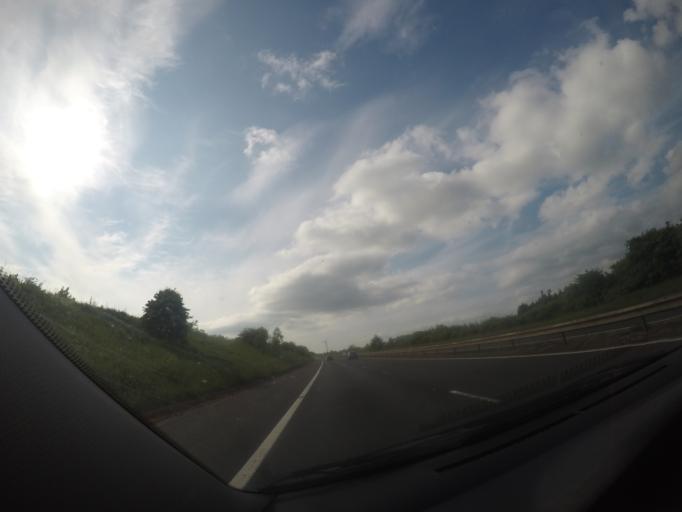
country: GB
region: Scotland
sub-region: South Lanarkshire
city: Lesmahagow
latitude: 55.6514
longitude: -3.8934
